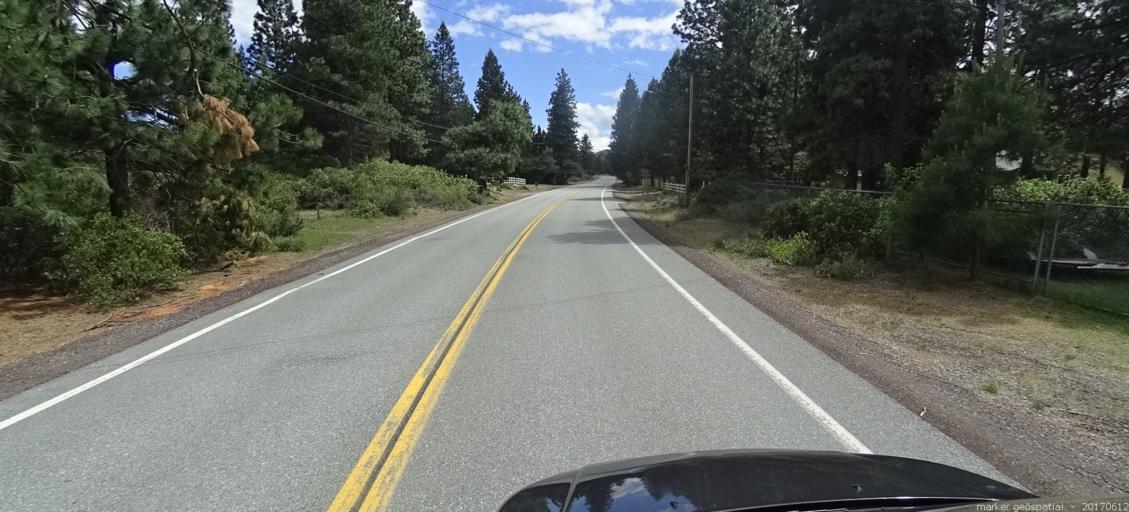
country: US
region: California
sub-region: Siskiyou County
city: Weed
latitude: 41.3598
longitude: -122.3763
